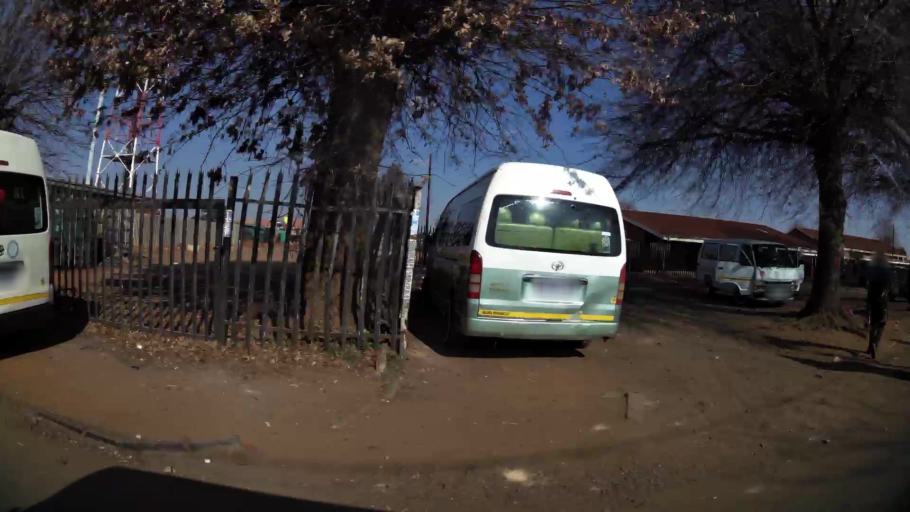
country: ZA
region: Gauteng
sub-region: Ekurhuleni Metropolitan Municipality
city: Brakpan
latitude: -26.1516
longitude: 28.4156
